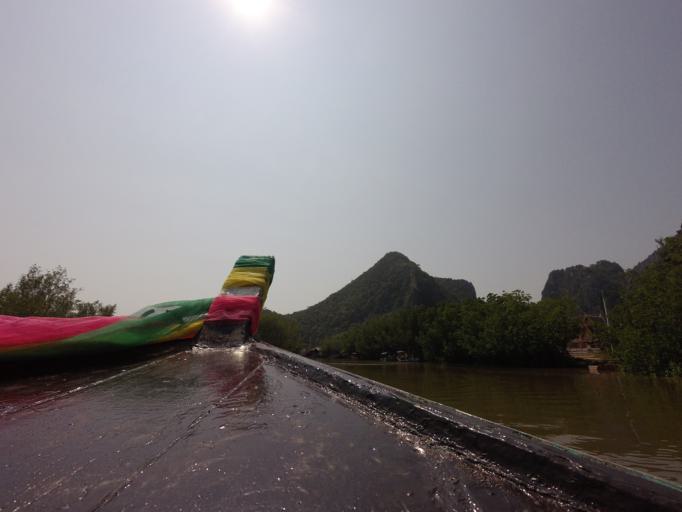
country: TH
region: Prachuap Khiri Khan
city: Kui Buri
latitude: 12.1366
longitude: 99.9612
